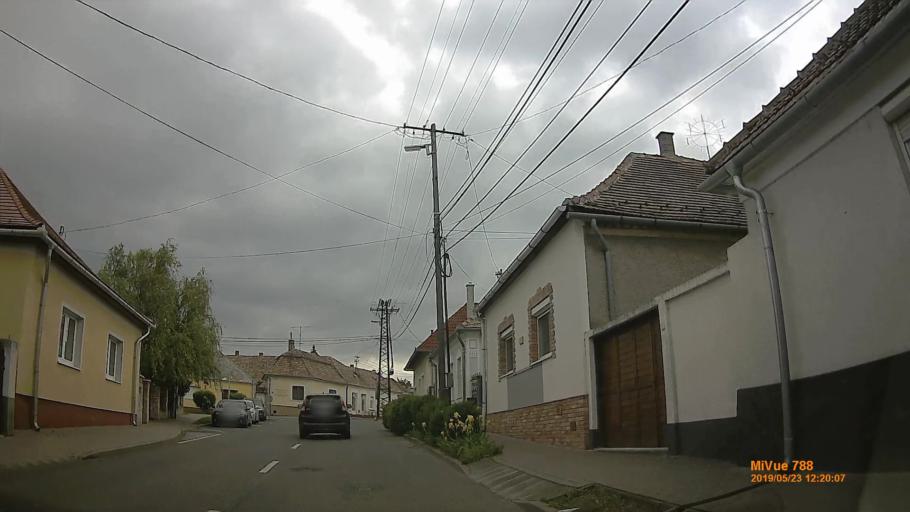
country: HU
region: Veszprem
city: Veszprem
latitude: 47.0912
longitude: 17.8996
